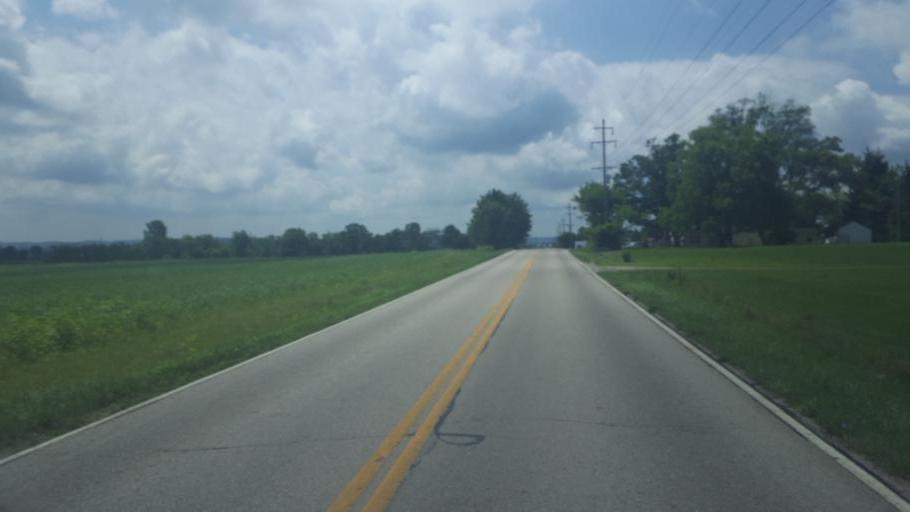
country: US
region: Ohio
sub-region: Ross County
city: Kingston
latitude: 39.5044
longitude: -82.7740
